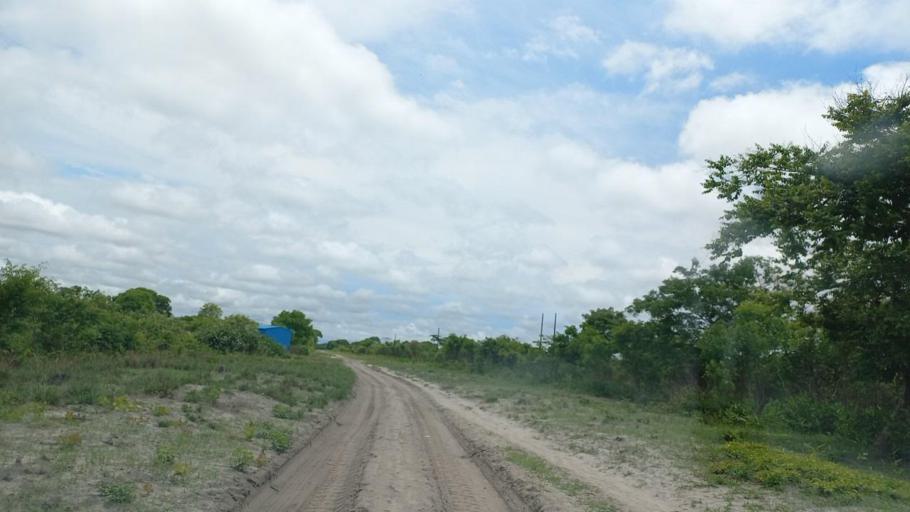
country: ZM
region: North-Western
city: Kabompo
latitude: -13.1824
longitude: 23.9504
